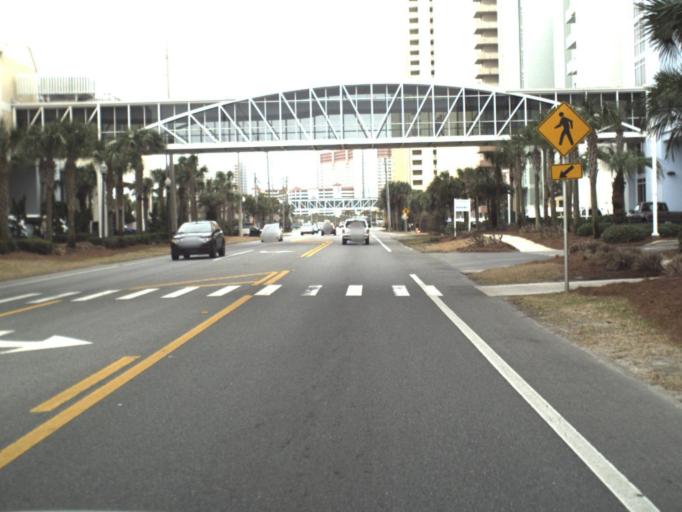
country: US
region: Florida
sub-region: Bay County
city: Panama City Beach
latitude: 30.1808
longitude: -85.8139
